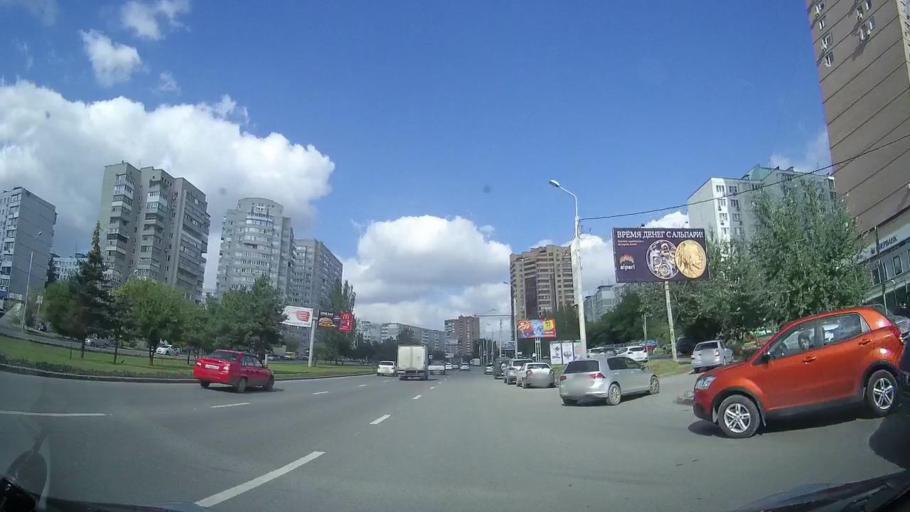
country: RU
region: Rostov
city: Severnyy
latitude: 47.2886
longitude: 39.6945
